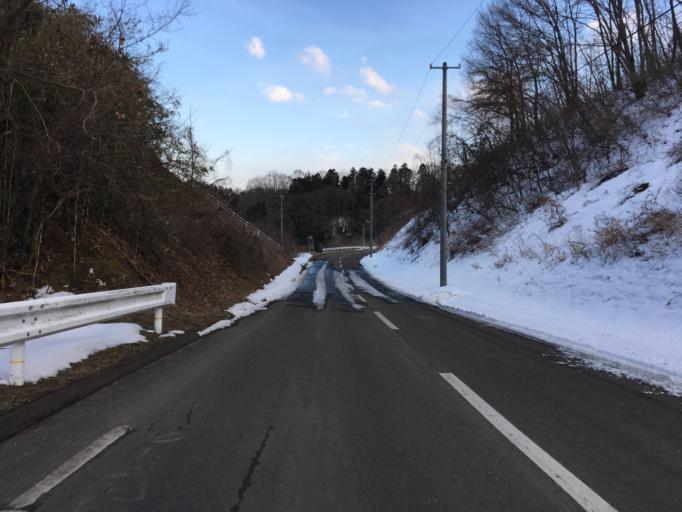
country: JP
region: Fukushima
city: Fukushima-shi
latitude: 37.6456
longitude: 140.5836
